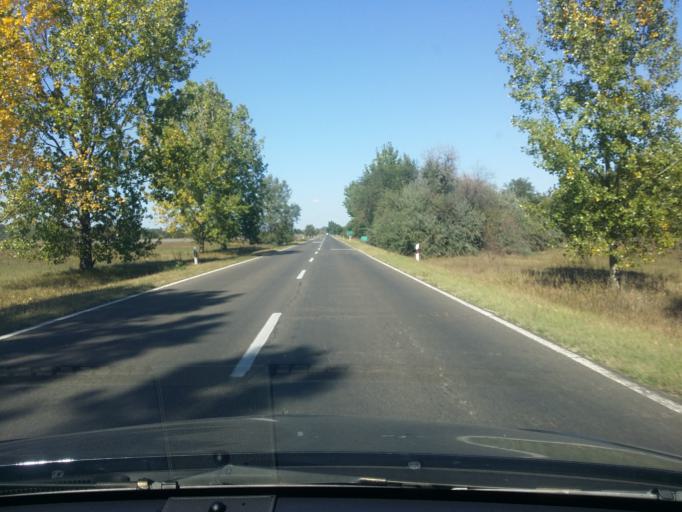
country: HU
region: Csongrad
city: Pusztaszer
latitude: 46.5543
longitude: 19.9477
